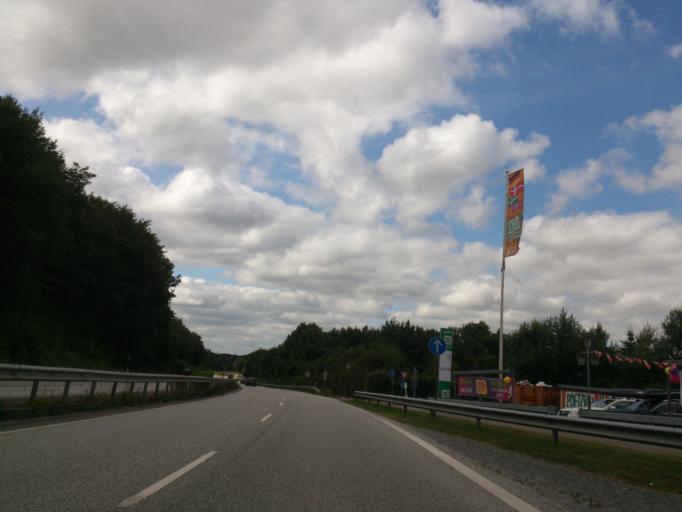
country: DK
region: South Denmark
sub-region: Aabenraa Kommune
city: Krusa
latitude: 54.8350
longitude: 9.4125
